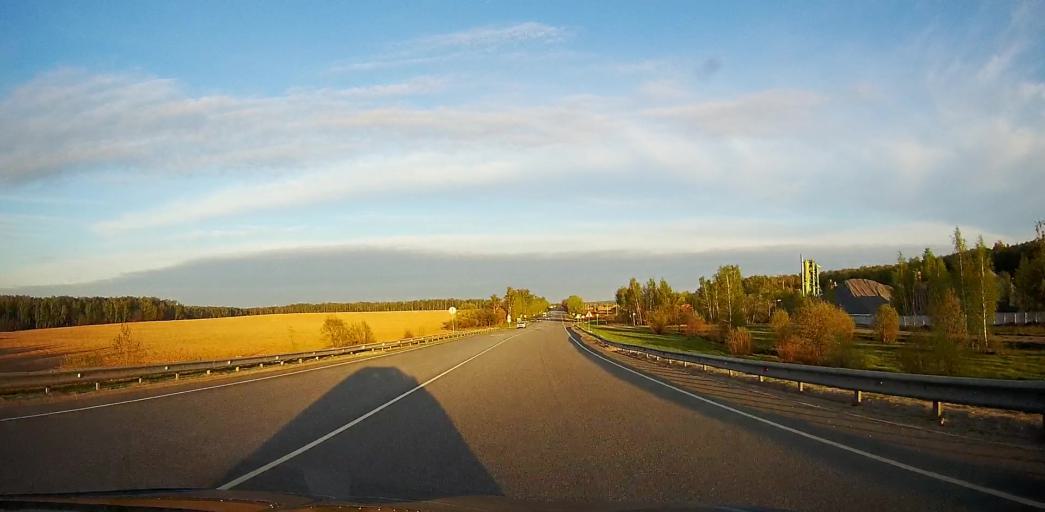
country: RU
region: Moskovskaya
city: Troitskoye
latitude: 55.2172
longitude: 38.5894
